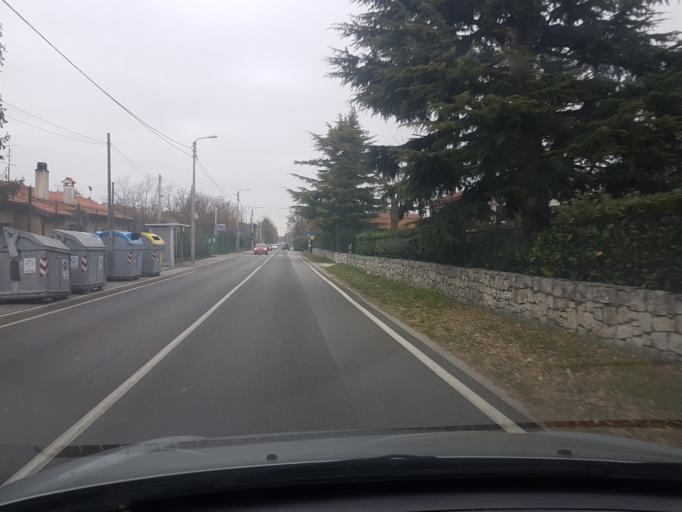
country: IT
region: Friuli Venezia Giulia
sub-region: Provincia di Trieste
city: Prosecco-Contovello
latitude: 45.7155
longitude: 13.7270
